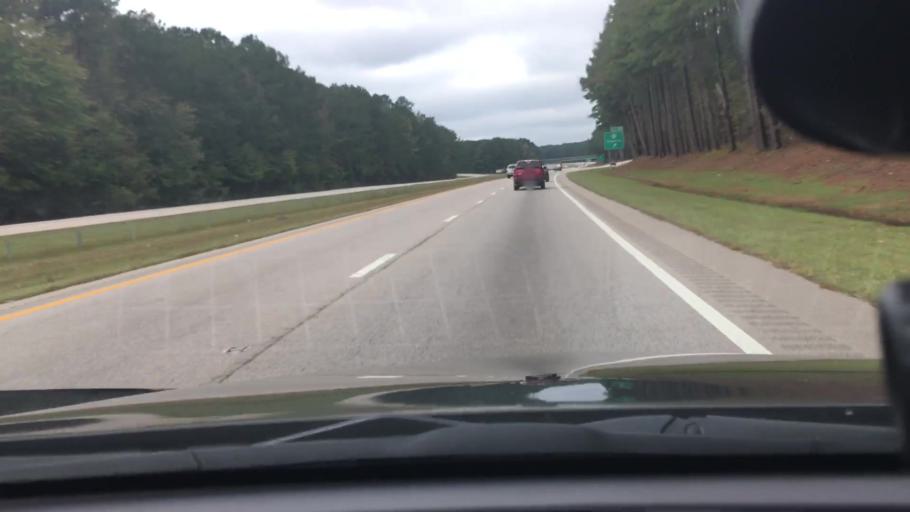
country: US
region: North Carolina
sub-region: Wake County
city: Zebulon
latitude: 35.8262
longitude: -78.2849
